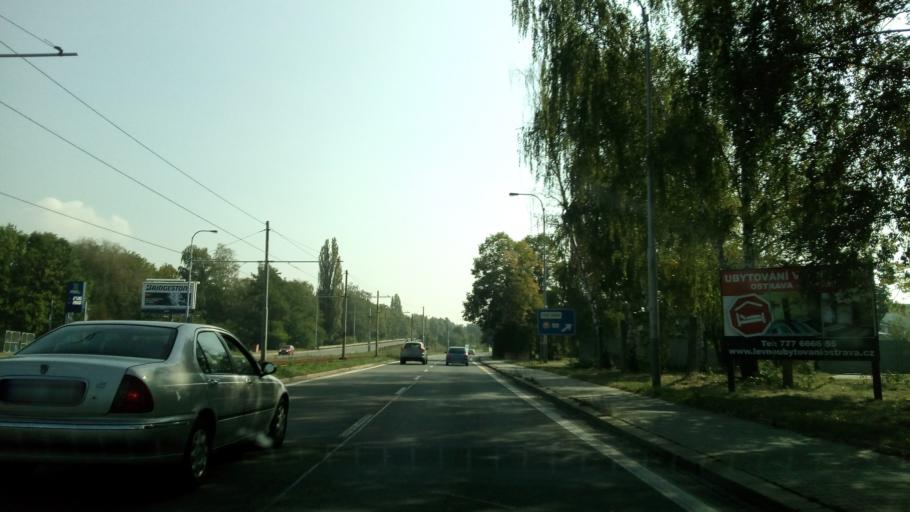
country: CZ
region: Moravskoslezsky
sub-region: Okres Ostrava-Mesto
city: Ostrava
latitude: 49.8133
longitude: 18.2404
